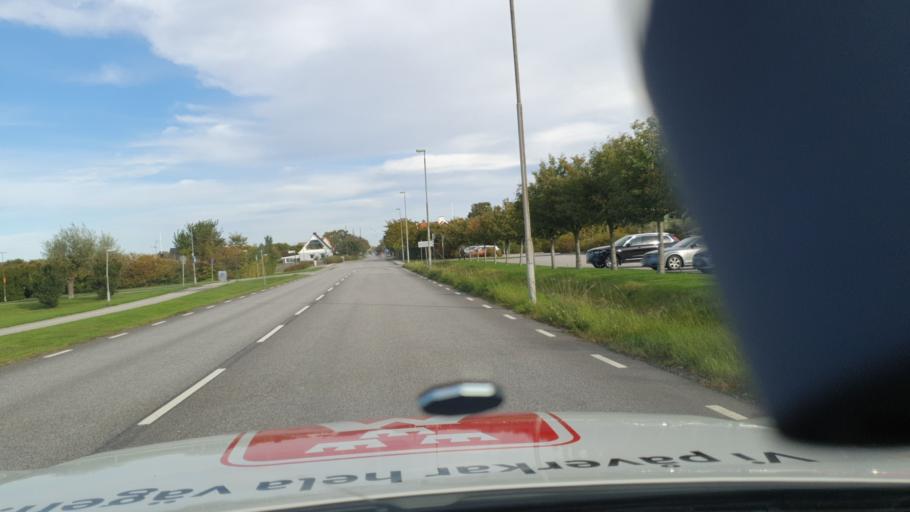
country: SE
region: Skane
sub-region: Malmo
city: Bunkeflostrand
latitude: 55.5509
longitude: 12.9179
